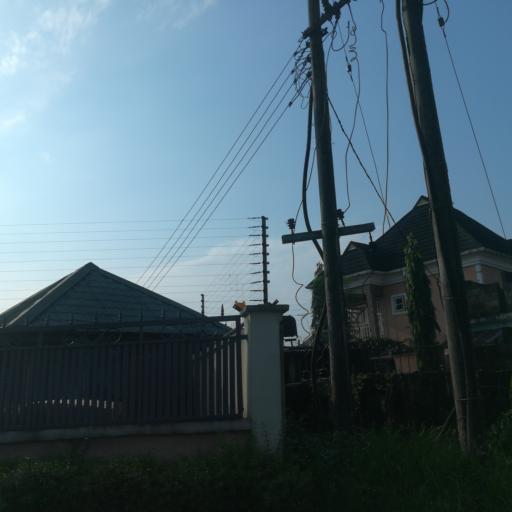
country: NG
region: Rivers
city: Port Harcourt
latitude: 4.8557
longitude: 6.9636
